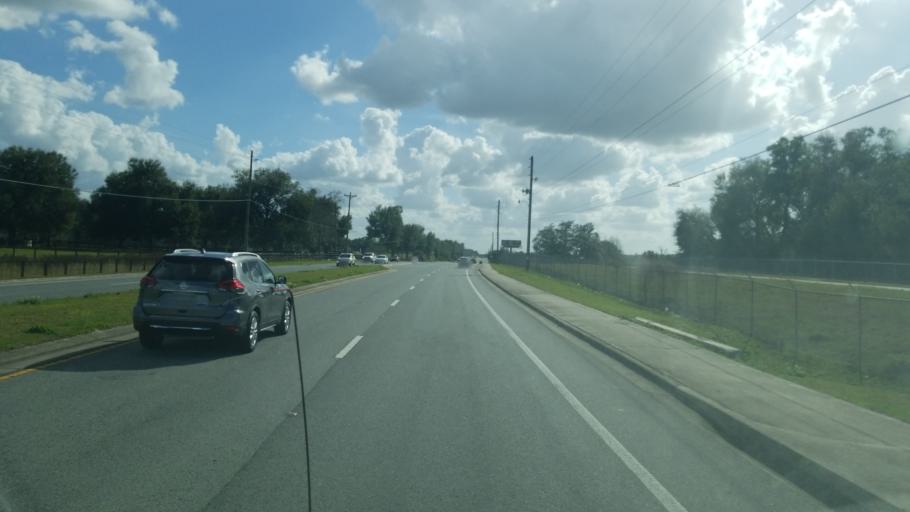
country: US
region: Florida
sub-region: Marion County
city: Ocala
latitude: 29.1588
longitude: -82.2188
